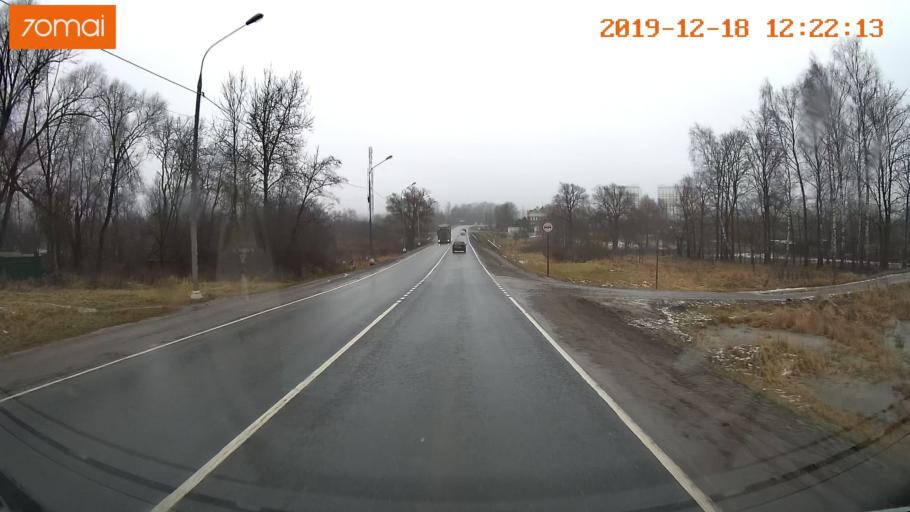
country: RU
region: Moskovskaya
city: Novopetrovskoye
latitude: 56.0039
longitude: 36.4789
